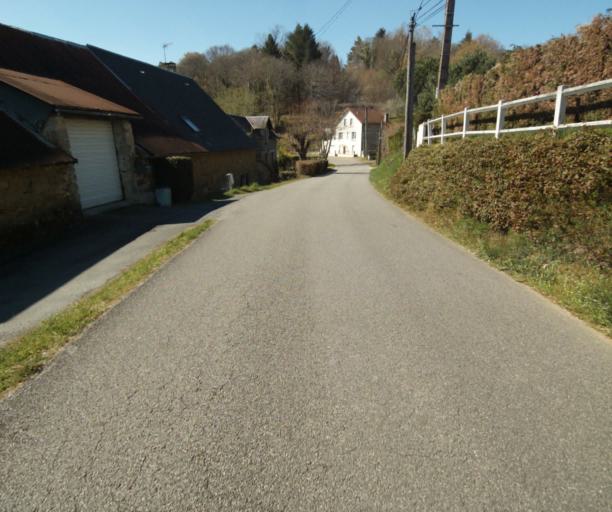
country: FR
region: Limousin
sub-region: Departement de la Correze
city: Tulle
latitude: 45.2592
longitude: 1.7382
